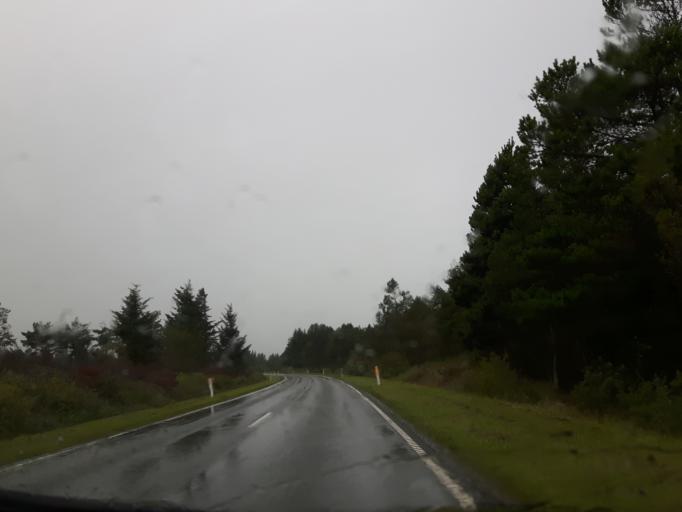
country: DK
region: North Denmark
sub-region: Thisted Kommune
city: Hanstholm
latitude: 57.0262
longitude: 8.4800
